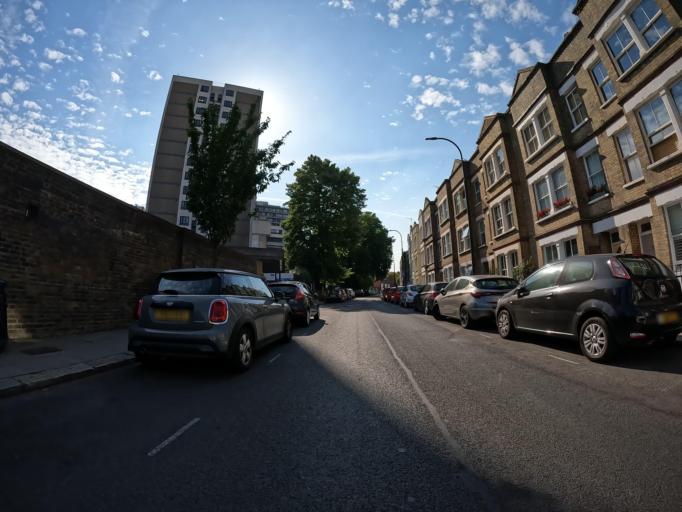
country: GB
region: England
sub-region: Greater London
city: Hendon
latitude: 51.5870
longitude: -0.2207
